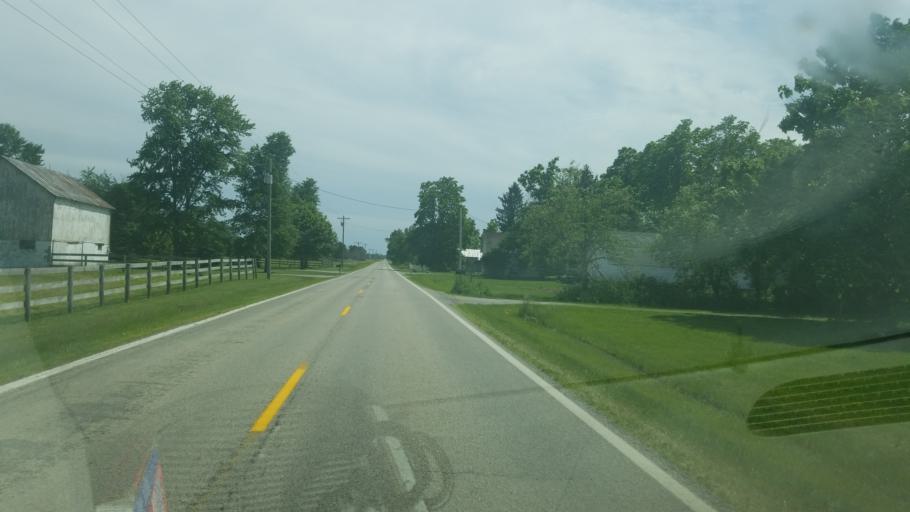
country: US
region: Ohio
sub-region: Morrow County
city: Cardington
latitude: 40.5099
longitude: -82.9629
